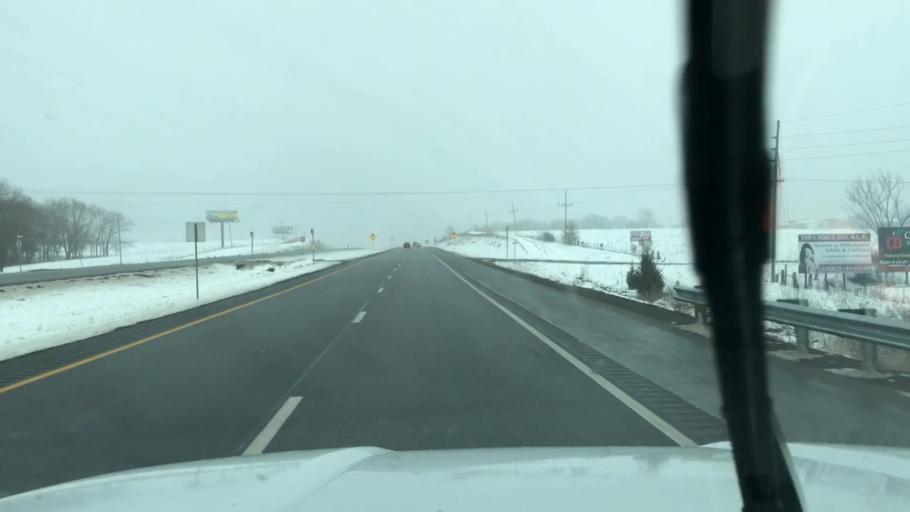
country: US
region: Missouri
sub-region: Clinton County
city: Cameron
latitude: 39.7539
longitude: -94.2635
